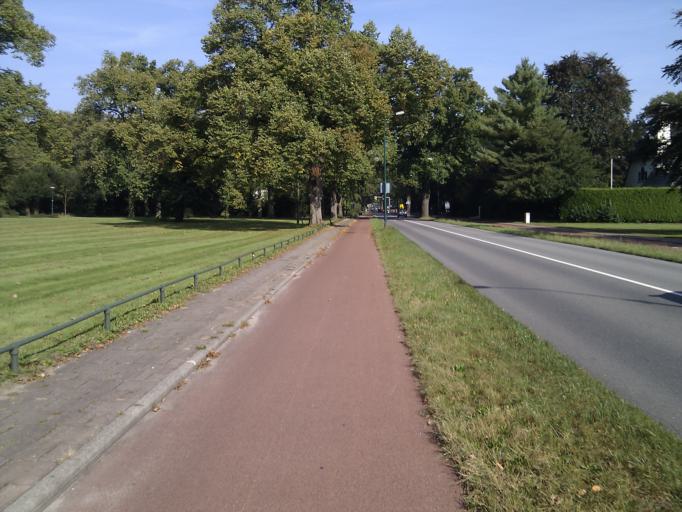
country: NL
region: Utrecht
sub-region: Gemeente De Bilt
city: De Bilt
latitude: 52.1203
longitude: 5.1974
